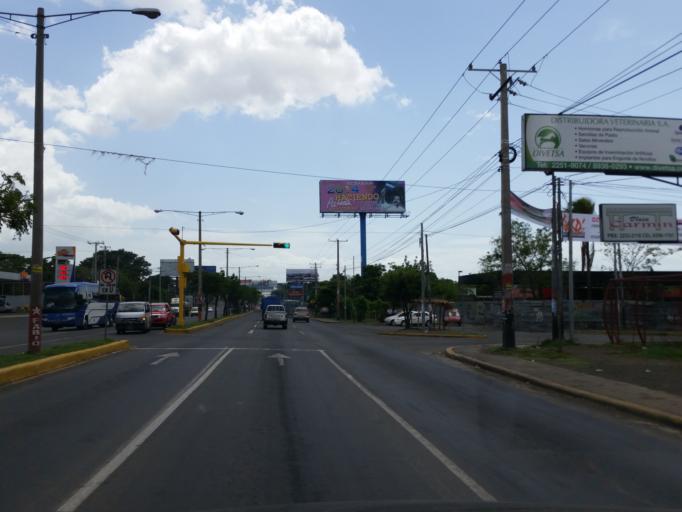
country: NI
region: Managua
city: Managua
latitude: 12.1473
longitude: -86.1874
